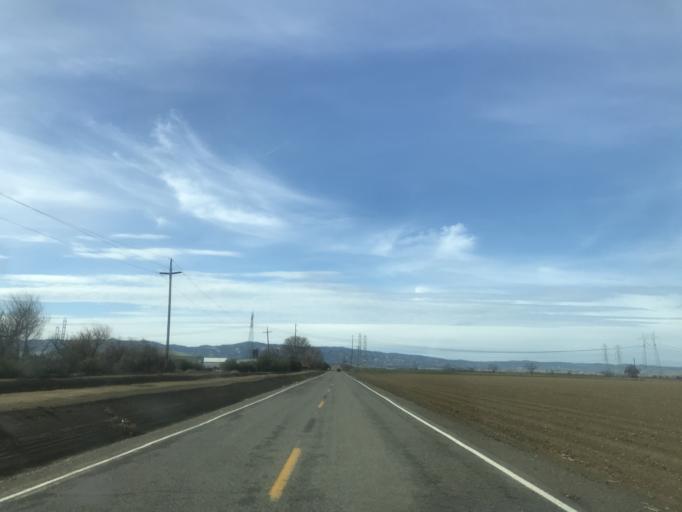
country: US
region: California
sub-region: Yolo County
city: Cottonwood
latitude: 38.6638
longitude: -121.9392
